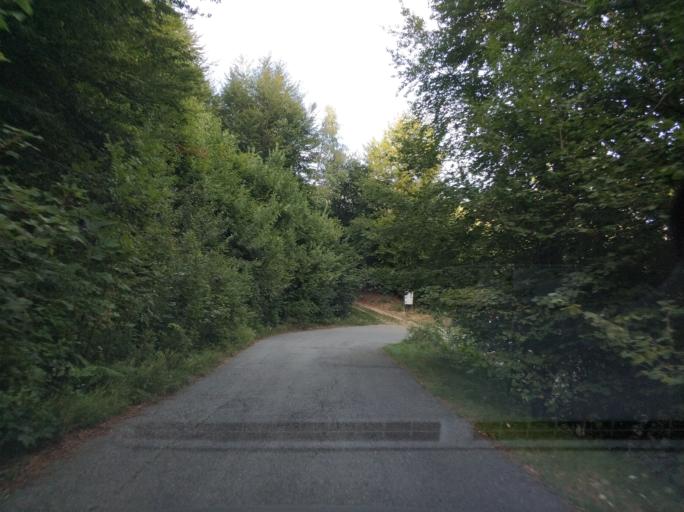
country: IT
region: Piedmont
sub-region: Provincia di Torino
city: Monastero di Lanzo
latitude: 45.3132
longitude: 7.4230
